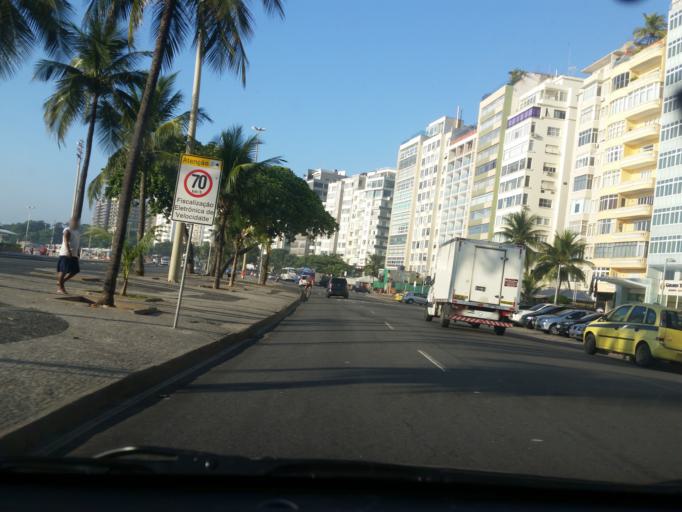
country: BR
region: Rio de Janeiro
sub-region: Rio De Janeiro
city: Rio de Janeiro
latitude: -22.9807
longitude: -43.1898
